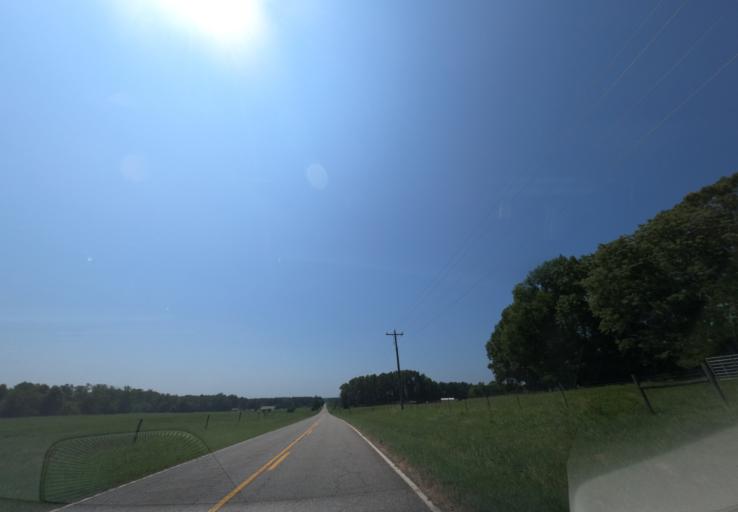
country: US
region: South Carolina
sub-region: Greenwood County
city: Greenwood
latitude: 34.0303
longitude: -82.1291
